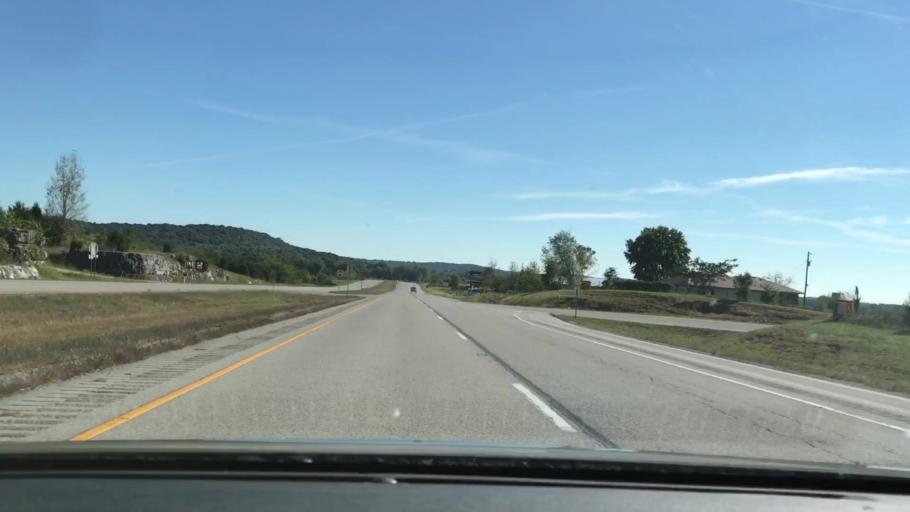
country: US
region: Kentucky
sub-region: Todd County
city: Elkton
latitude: 36.8458
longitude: -87.2887
